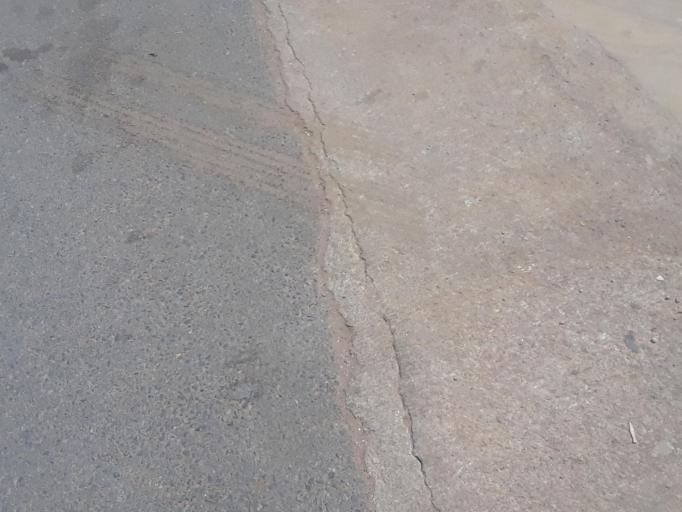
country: ZM
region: Lusaka
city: Lusaka
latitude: -15.3582
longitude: 28.2812
